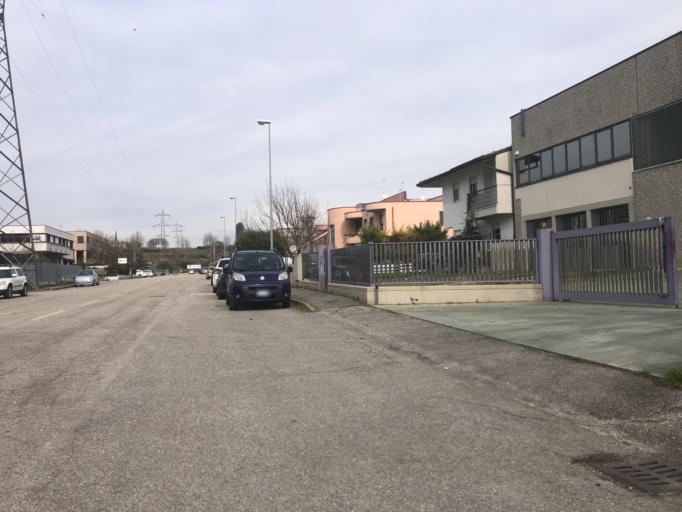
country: IT
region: Veneto
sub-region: Provincia di Verona
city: San Giorgio in Salici
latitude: 45.4377
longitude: 10.8052
